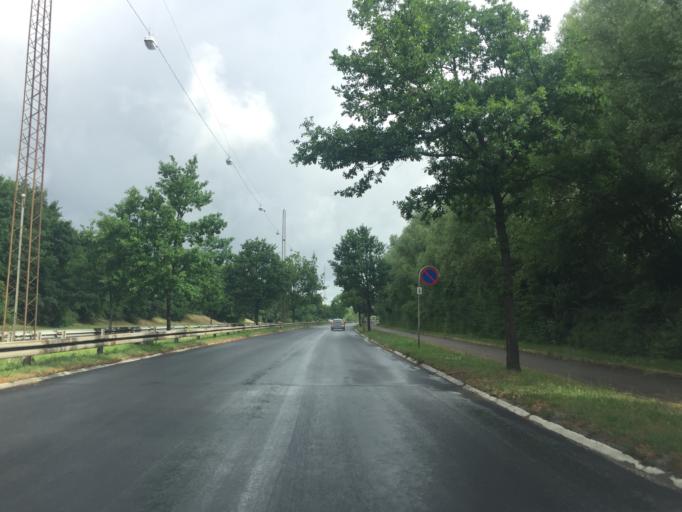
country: DK
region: Capital Region
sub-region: Hvidovre Kommune
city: Hvidovre
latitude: 55.6587
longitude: 12.4544
